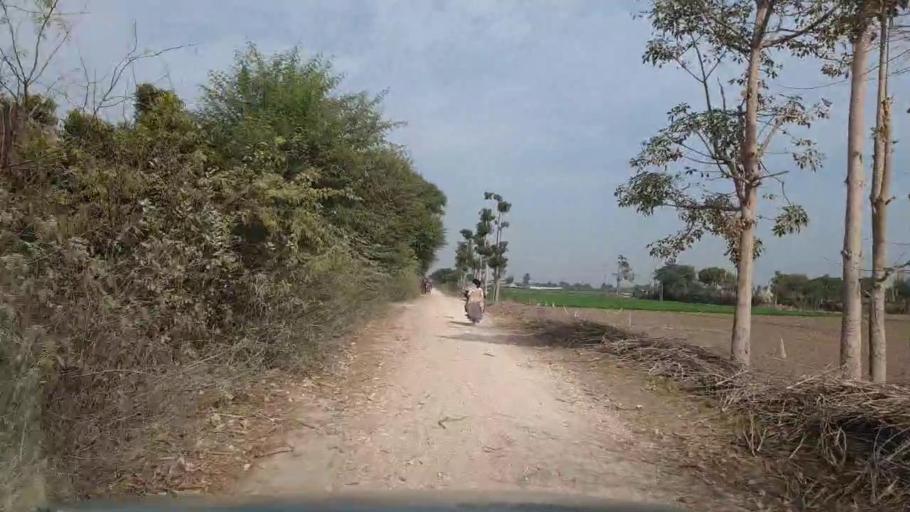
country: PK
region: Sindh
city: Tando Jam
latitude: 25.5250
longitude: 68.5620
